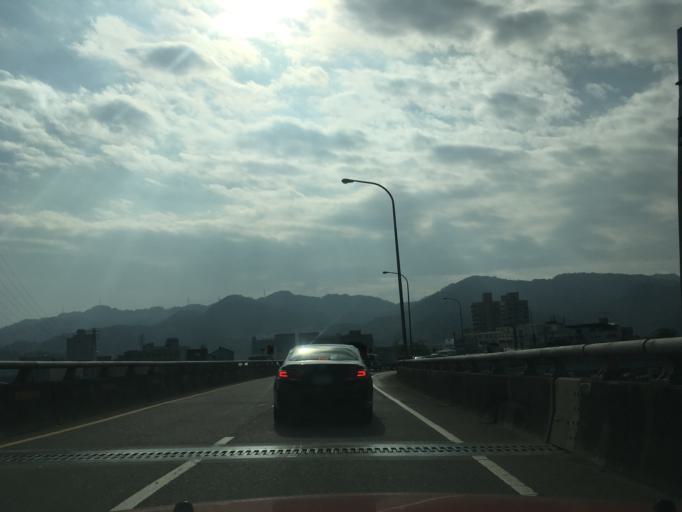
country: TW
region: Taipei
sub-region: Taipei
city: Banqiao
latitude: 24.9708
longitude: 121.4334
